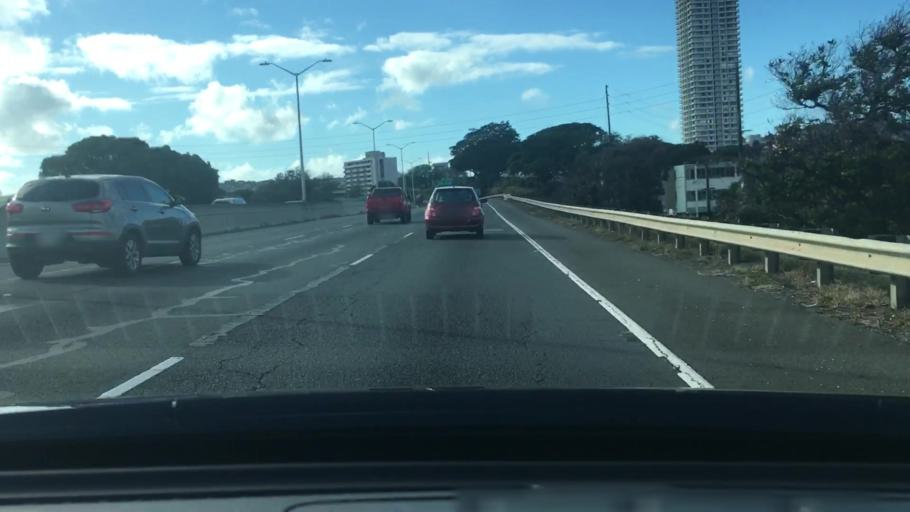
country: US
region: Hawaii
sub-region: Honolulu County
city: Honolulu
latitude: 21.2931
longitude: -157.8200
